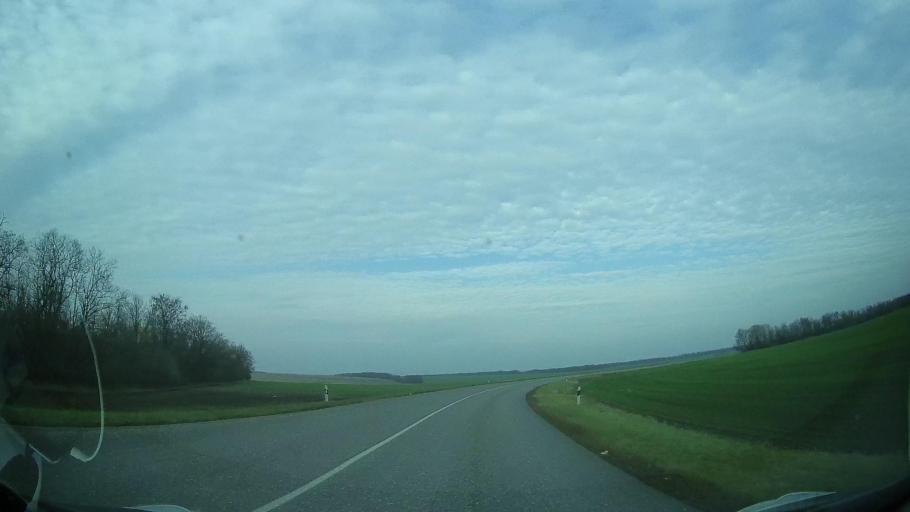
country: RU
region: Rostov
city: Zernograd
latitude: 46.9637
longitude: 40.3670
